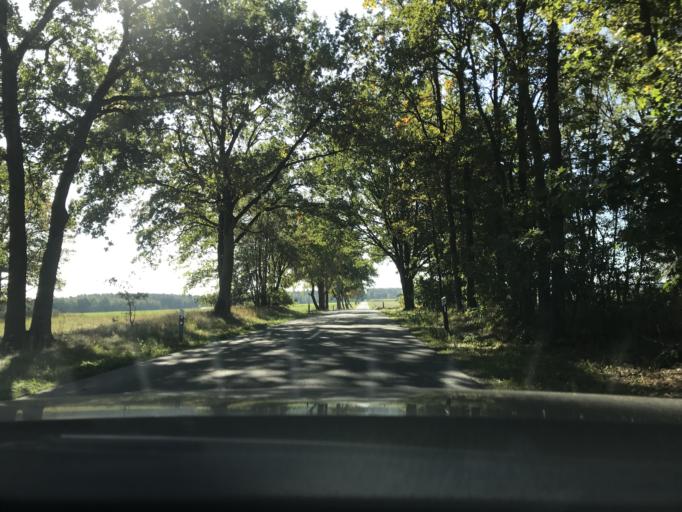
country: DE
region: Lower Saxony
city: Gerdau
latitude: 52.9494
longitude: 10.4007
